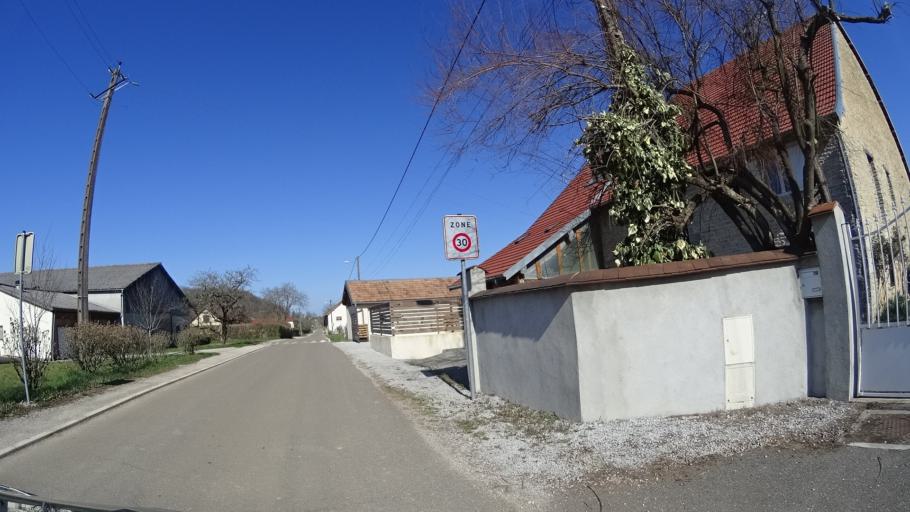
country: FR
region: Franche-Comte
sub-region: Departement du Doubs
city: Ornans
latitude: 47.1451
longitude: 6.0862
